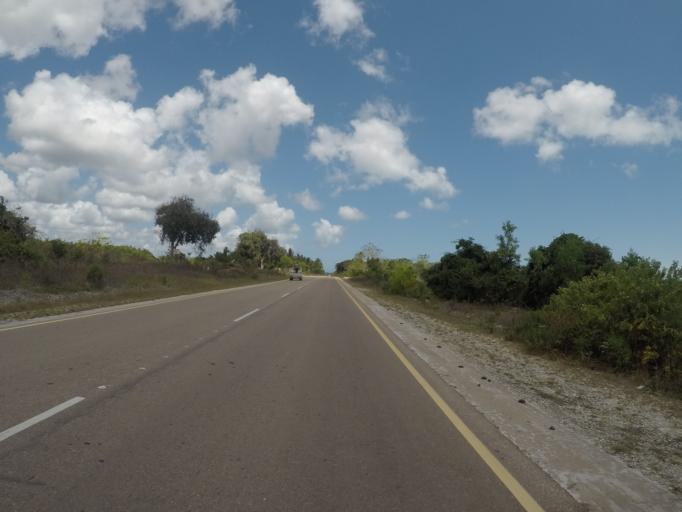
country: TZ
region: Zanzibar Central/South
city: Koani
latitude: -6.2650
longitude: 39.3607
